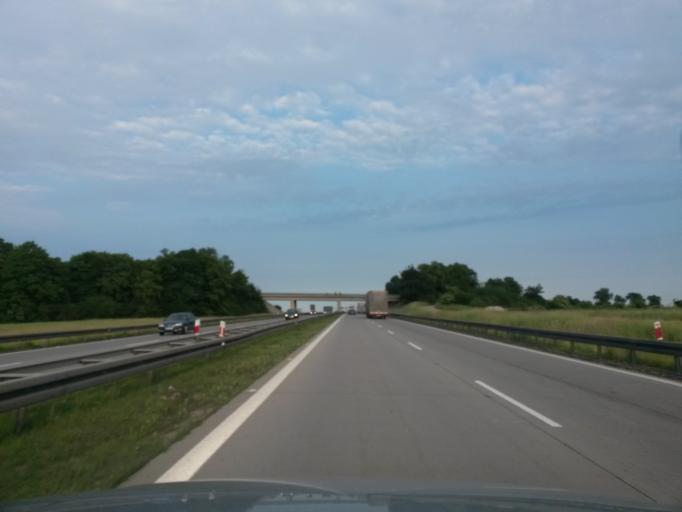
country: PL
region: Lower Silesian Voivodeship
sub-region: Powiat sredzki
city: Ciechow
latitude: 51.0377
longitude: 16.6132
